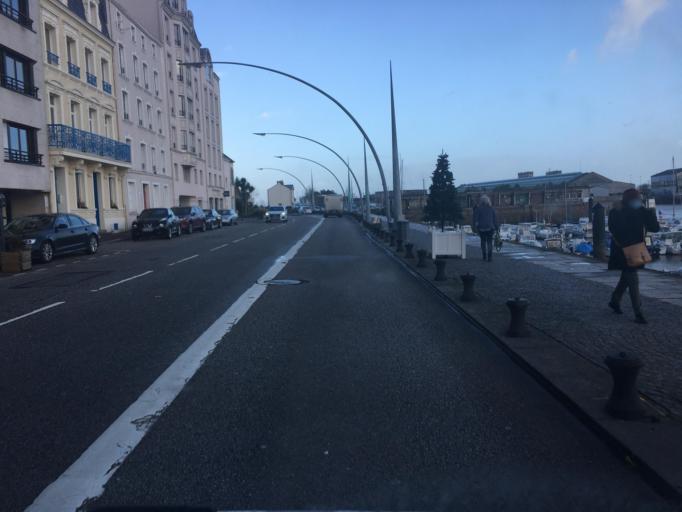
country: FR
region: Lower Normandy
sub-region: Departement de la Manche
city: Cherbourg-Octeville
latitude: 49.6406
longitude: -1.6213
